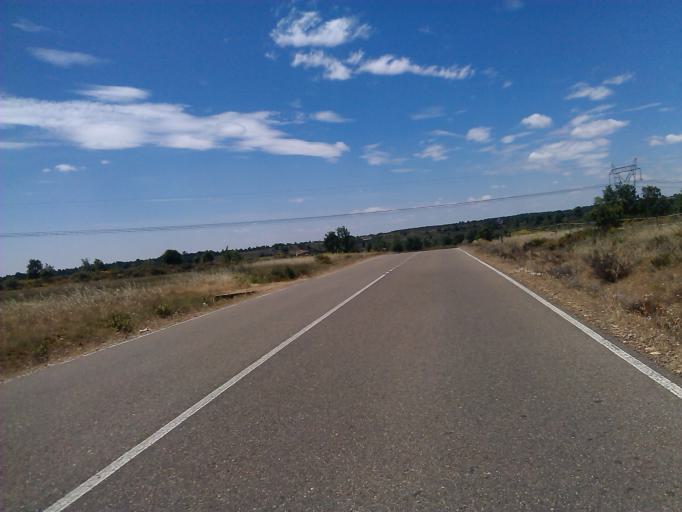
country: ES
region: Castille and Leon
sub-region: Provincia de Leon
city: Valverde de la Virgen
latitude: 42.5621
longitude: -5.6566
